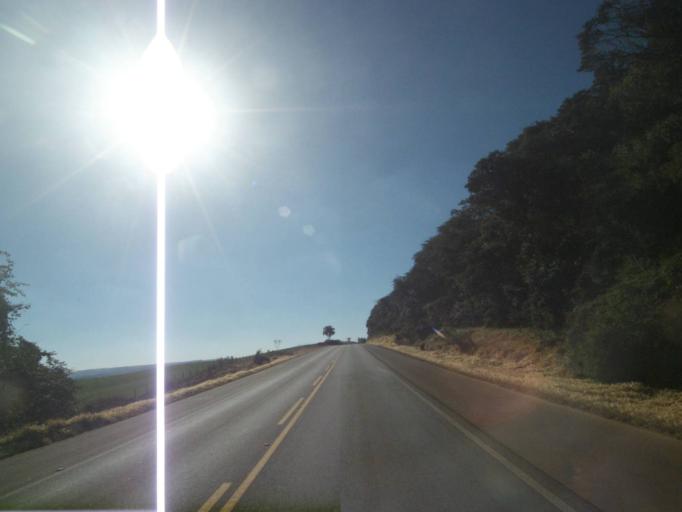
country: BR
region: Parana
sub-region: Tibagi
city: Tibagi
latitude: -24.7122
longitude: -50.4496
